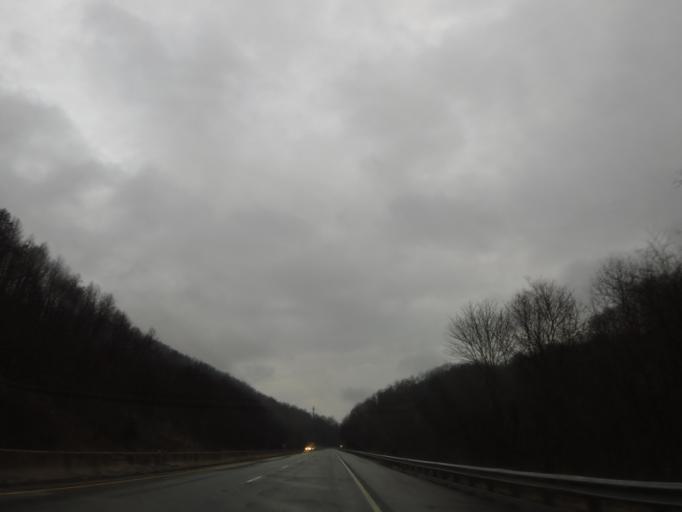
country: US
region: North Carolina
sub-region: Henderson County
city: Flat Rock
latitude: 35.1710
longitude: -82.4632
